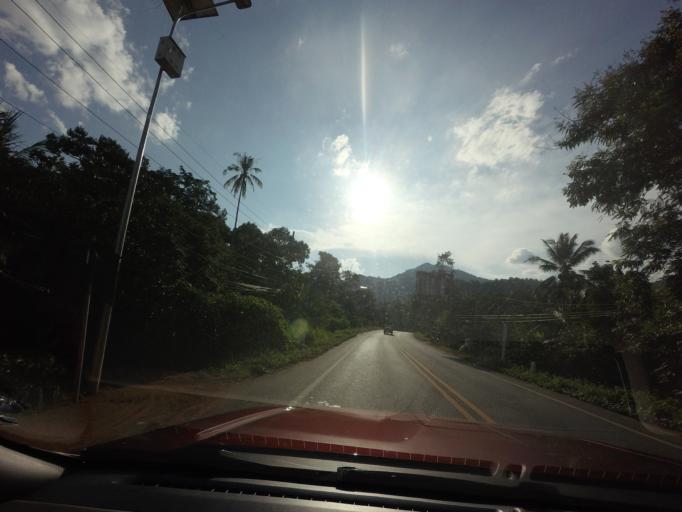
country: TH
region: Yala
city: Ban Nang Sata
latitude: 6.2349
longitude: 101.2088
